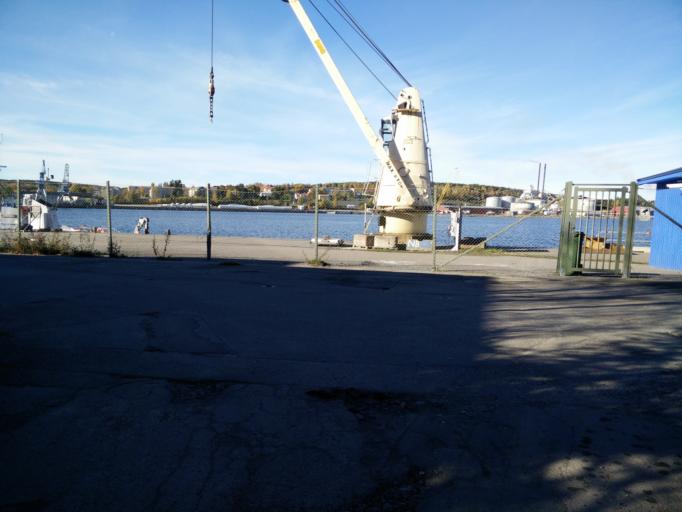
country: SE
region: Vaesternorrland
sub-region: Haernoesands Kommun
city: Haernoesand
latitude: 62.6385
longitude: 17.9468
